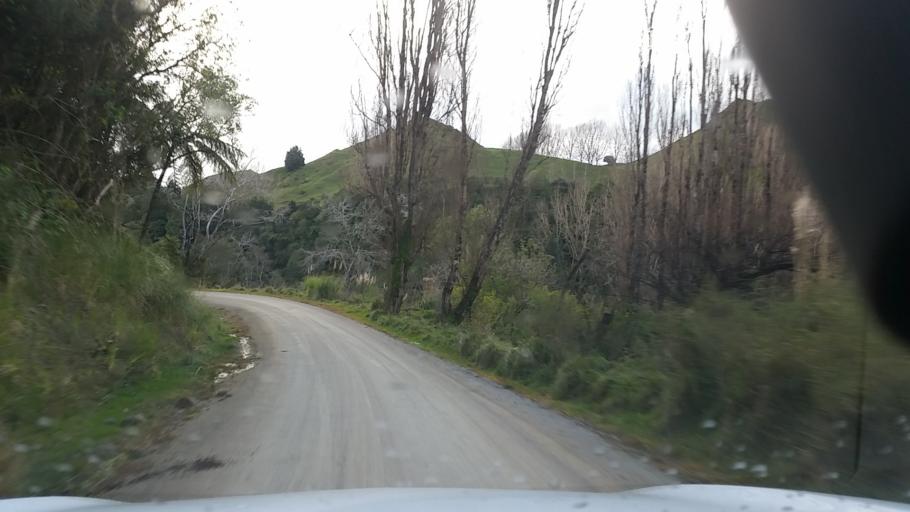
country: NZ
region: Taranaki
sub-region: South Taranaki District
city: Patea
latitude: -39.5575
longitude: 174.8056
